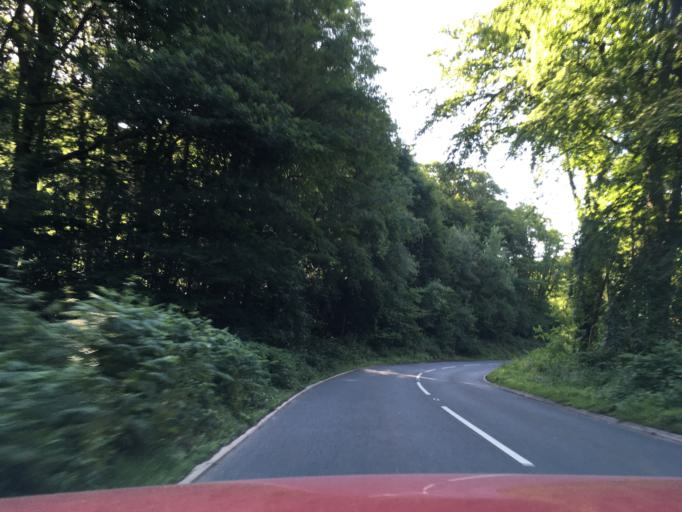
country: GB
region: England
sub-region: Gloucestershire
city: Lydney
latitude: 51.7409
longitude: -2.5414
